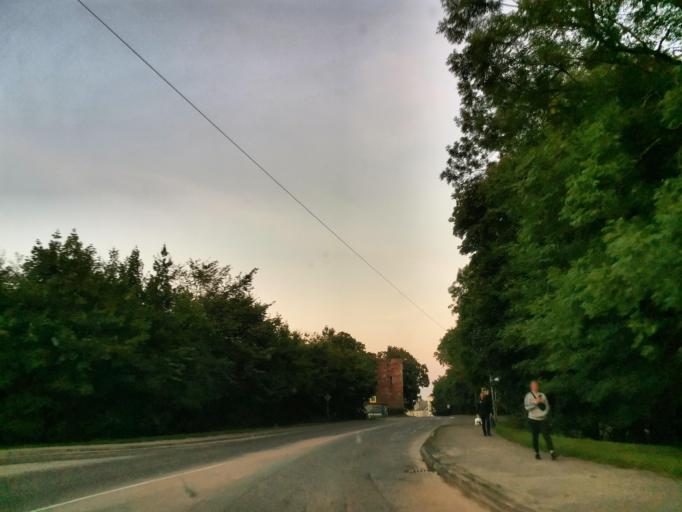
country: RU
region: Kaliningrad
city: Chernyakhovsk
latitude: 54.6390
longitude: 21.8047
